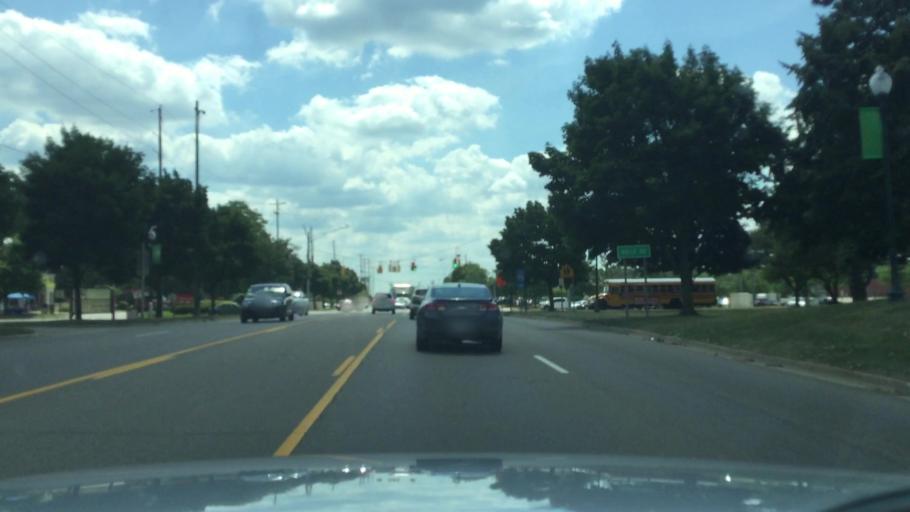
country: US
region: Michigan
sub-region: Genesee County
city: Grand Blanc
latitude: 42.9217
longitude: -83.6228
